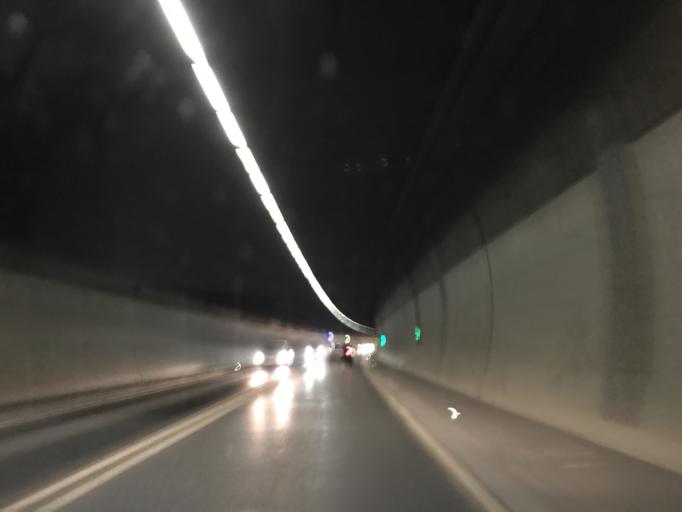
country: DE
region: Baden-Wuerttemberg
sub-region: Regierungsbezirk Stuttgart
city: Stuttgart
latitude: 48.7589
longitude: 9.1672
